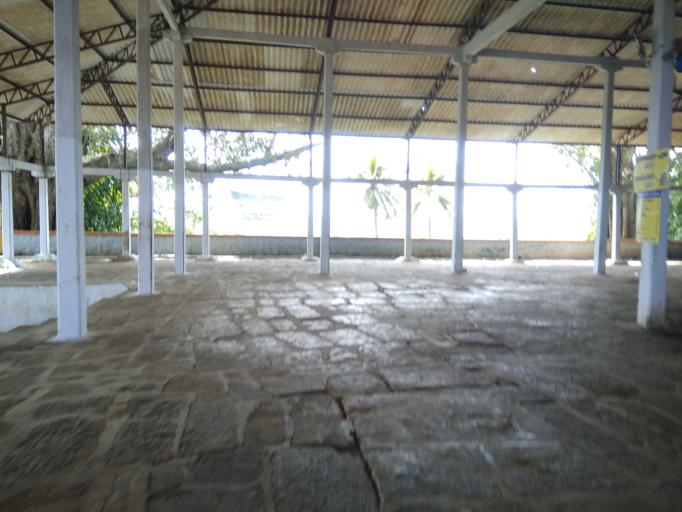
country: IN
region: Kerala
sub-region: Palakkad district
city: Ottappalam
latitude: 10.7407
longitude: 76.4307
